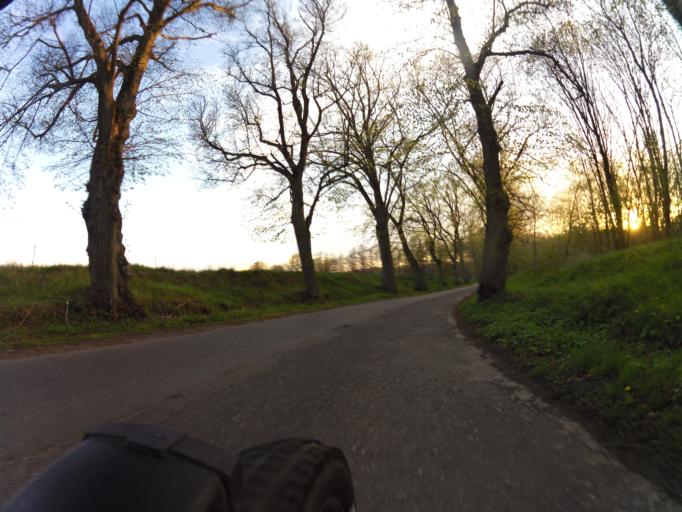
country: PL
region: West Pomeranian Voivodeship
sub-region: Powiat lobeski
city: Lobez
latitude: 53.6963
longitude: 15.6440
